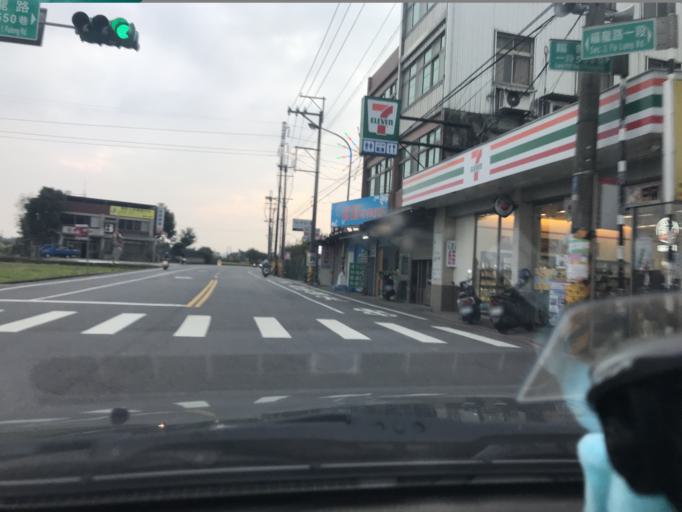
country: TW
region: Taiwan
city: Daxi
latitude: 24.8965
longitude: 121.2266
